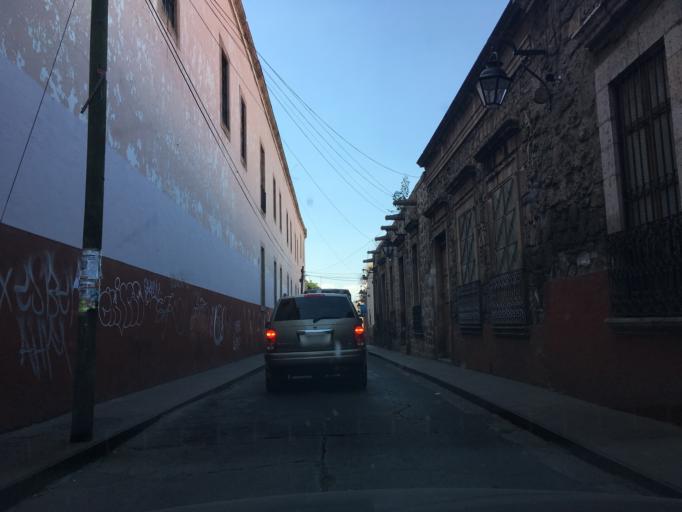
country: MX
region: Michoacan
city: Morelia
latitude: 19.7057
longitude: -101.1881
